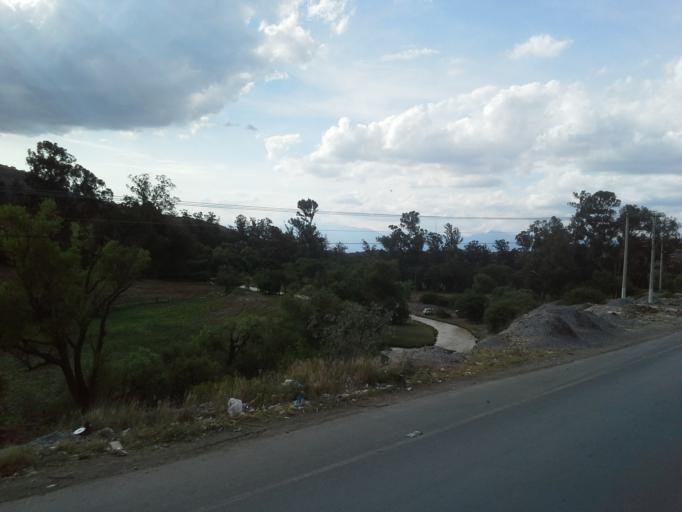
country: BO
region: Cochabamba
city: Cochabamba
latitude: -17.4953
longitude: -66.0921
